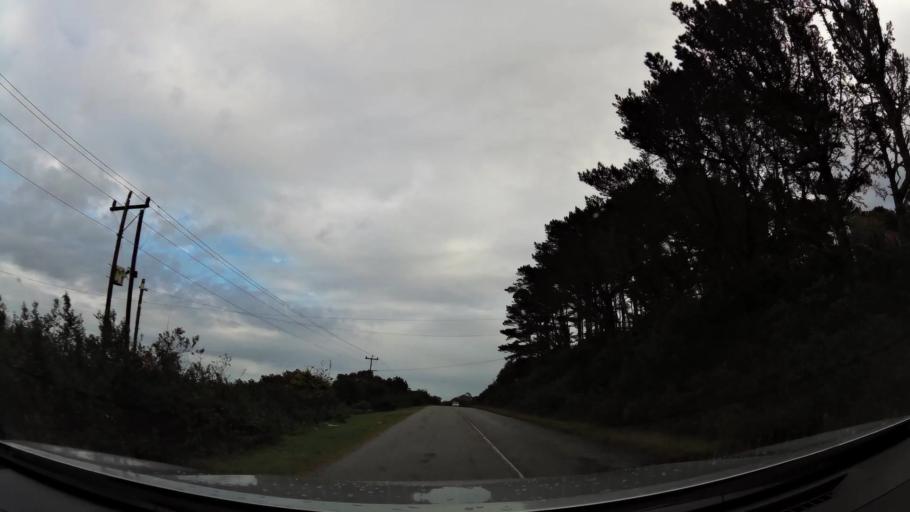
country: ZA
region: Eastern Cape
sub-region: Nelson Mandela Bay Metropolitan Municipality
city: Port Elizabeth
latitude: -34.0076
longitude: 25.4853
